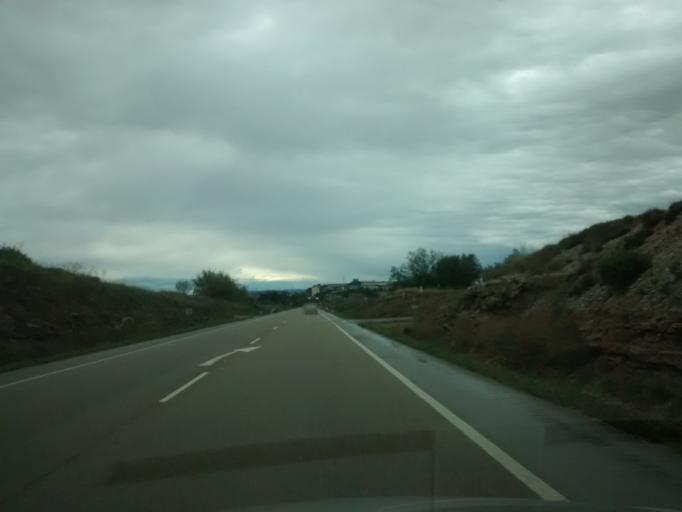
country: ES
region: Aragon
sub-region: Provincia de Zaragoza
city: Caspe
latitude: 41.2183
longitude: -0.0147
